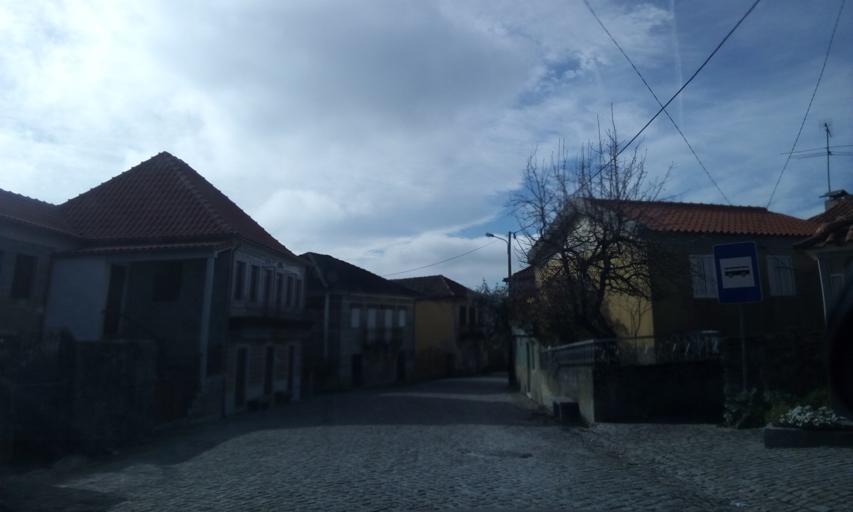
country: PT
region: Guarda
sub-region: Aguiar da Beira
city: Aguiar da Beira
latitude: 40.7328
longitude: -7.5560
